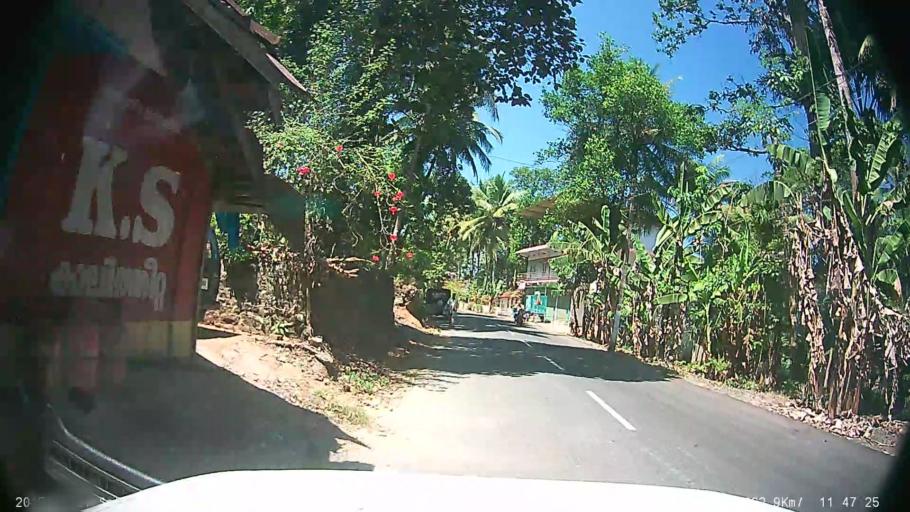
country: IN
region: Kerala
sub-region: Kottayam
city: Lalam
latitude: 9.7749
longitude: 76.7160
